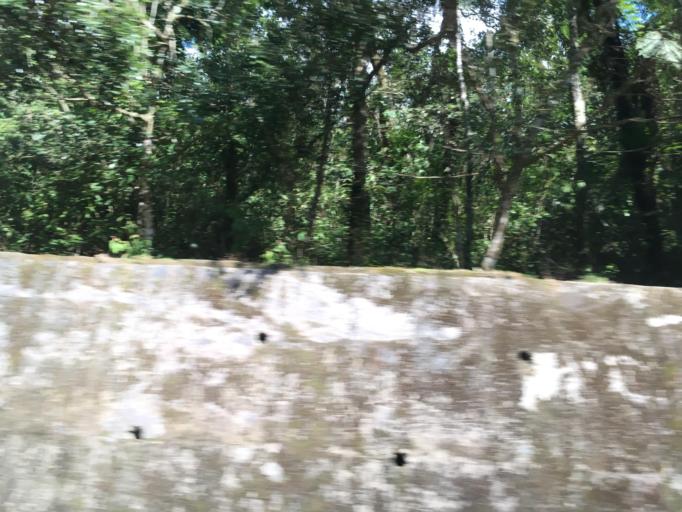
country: TW
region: Taiwan
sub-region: Yilan
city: Yilan
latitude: 24.7560
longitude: 121.5925
